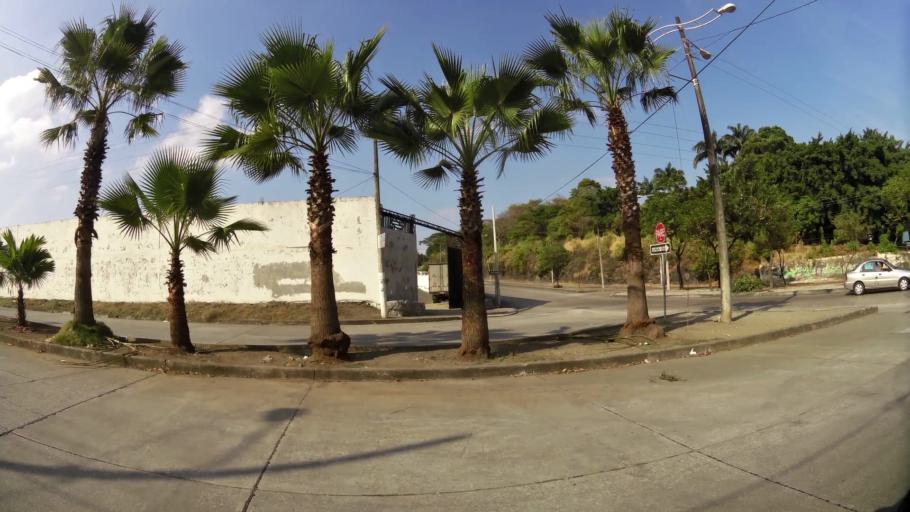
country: EC
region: Guayas
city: Guayaquil
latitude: -2.1369
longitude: -79.9246
